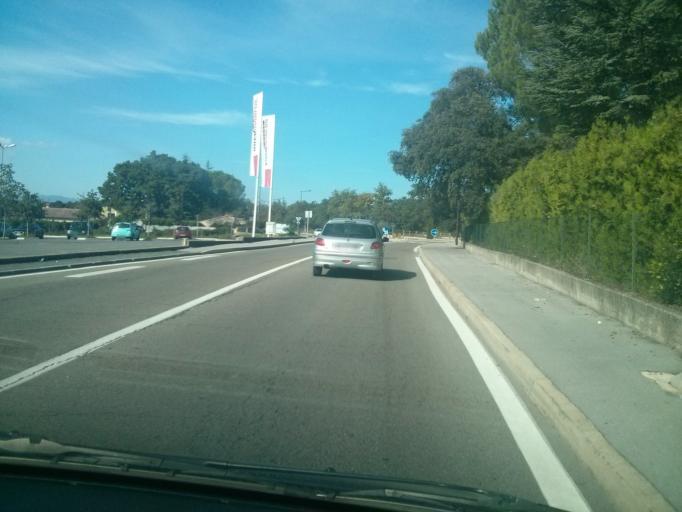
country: FR
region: Languedoc-Roussillon
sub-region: Departement du Gard
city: Quissac
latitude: 43.9162
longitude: 3.9940
